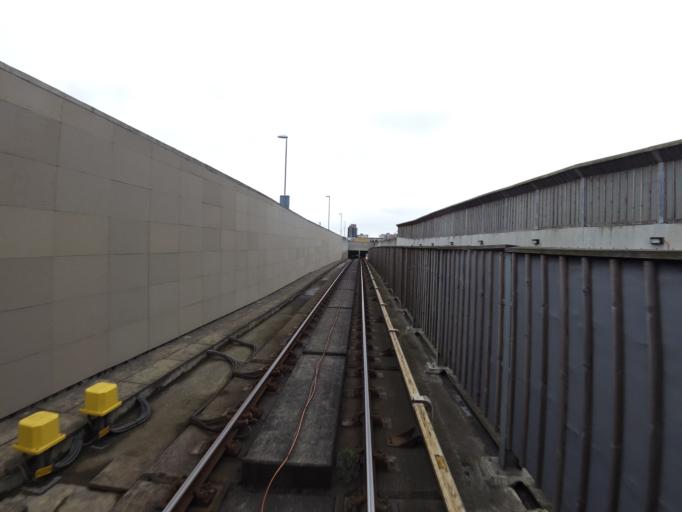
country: GB
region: England
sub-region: Greater London
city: Woolwich
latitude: 51.5021
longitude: 0.0634
